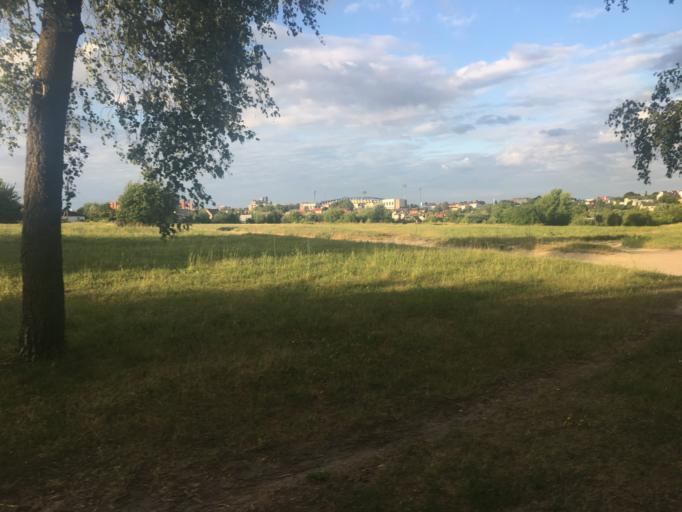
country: BY
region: Grodnenskaya
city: Hrodna
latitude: 53.6834
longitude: 23.8071
